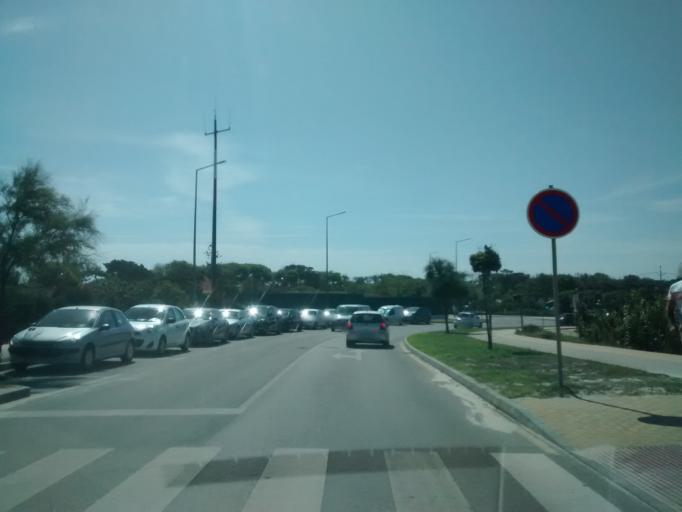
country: PT
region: Coimbra
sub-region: Mira
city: Mira
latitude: 40.4512
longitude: -8.8031
